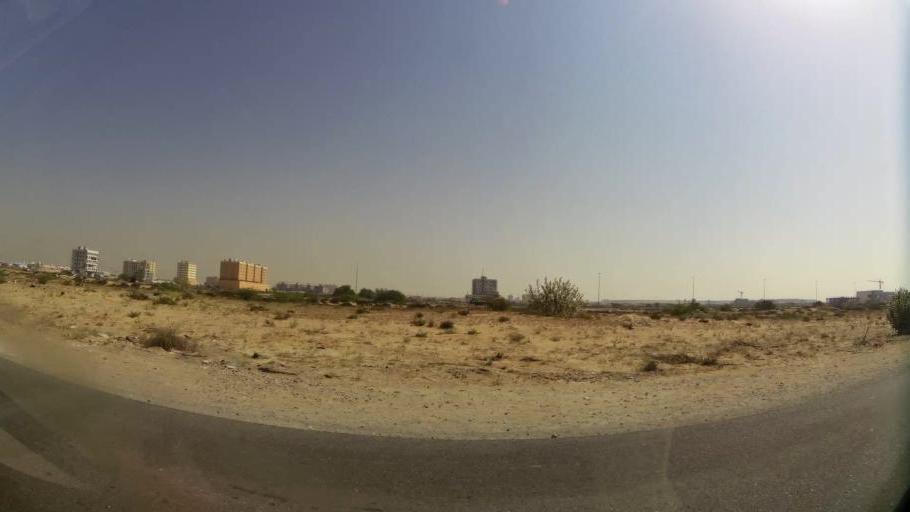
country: AE
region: Ajman
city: Ajman
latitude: 25.4186
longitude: 55.5368
